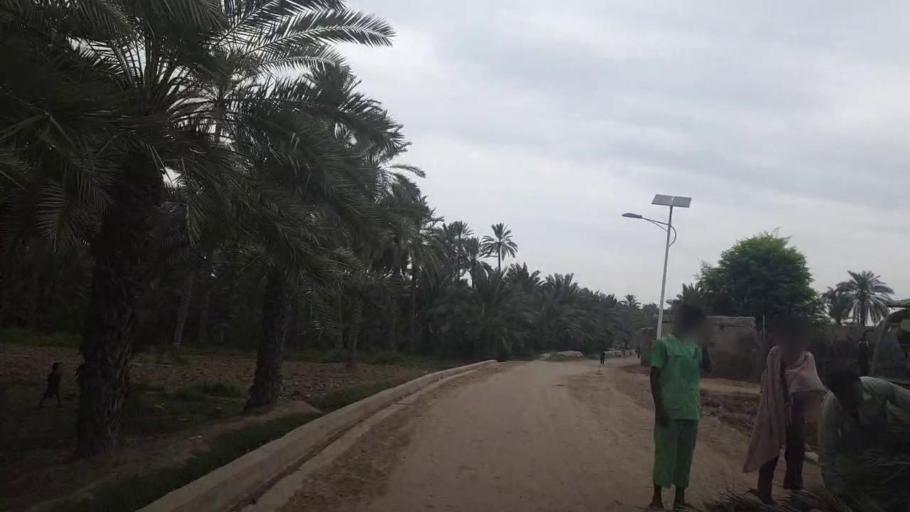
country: PK
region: Sindh
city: Khairpur
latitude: 27.5787
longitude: 68.7449
